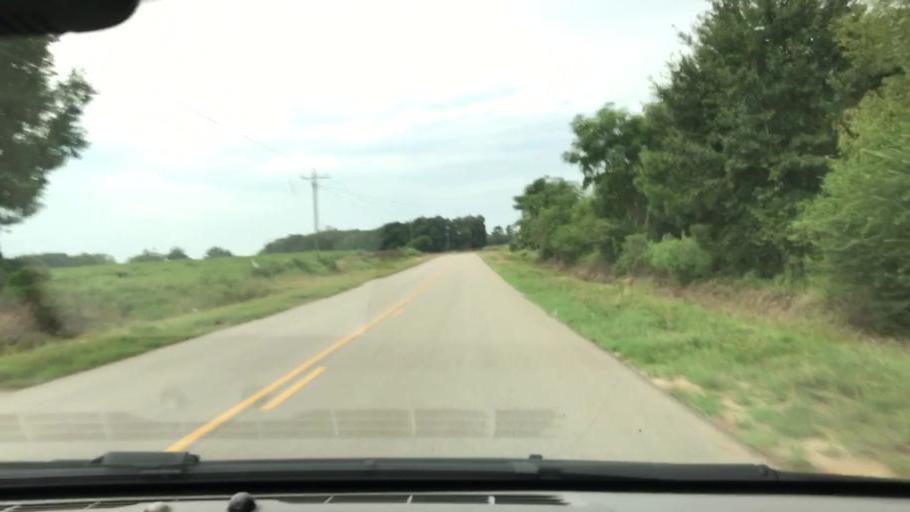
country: US
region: Alabama
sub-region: Houston County
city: Ashford
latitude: 31.2279
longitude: -85.1825
